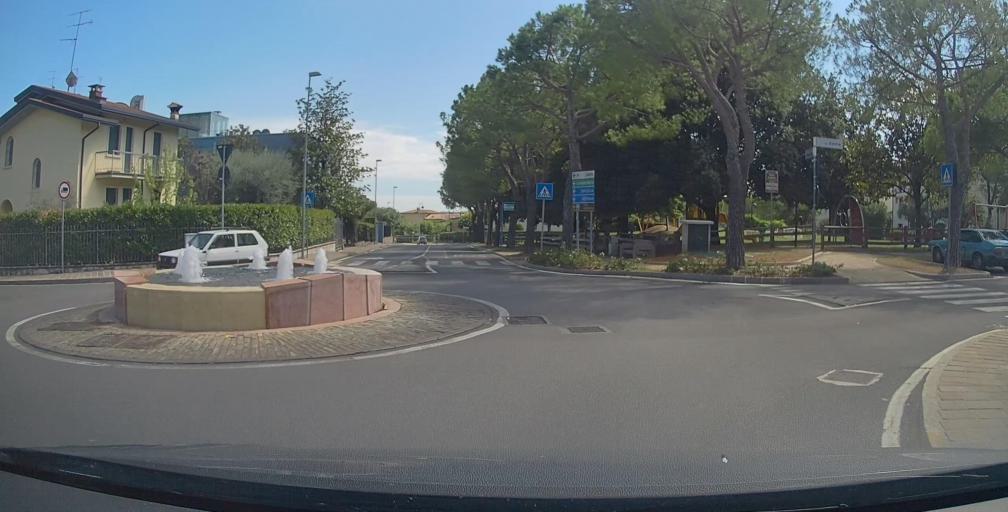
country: IT
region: Lombardy
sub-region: Provincia di Brescia
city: San Martino della Battaglia
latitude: 45.4638
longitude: 10.6065
